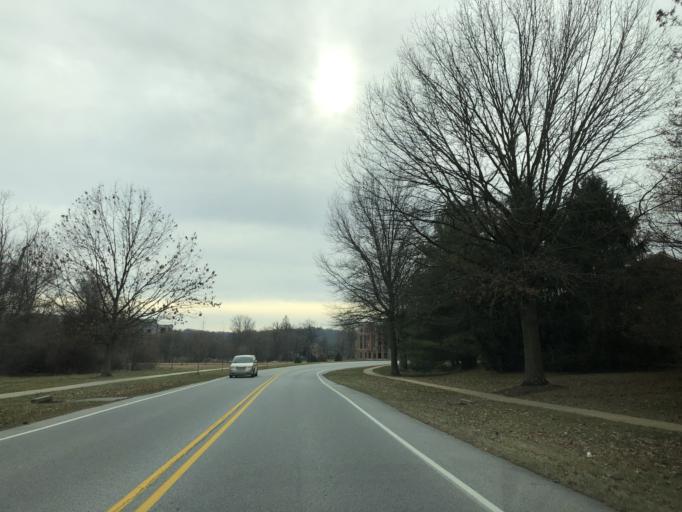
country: US
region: Pennsylvania
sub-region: Chester County
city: Exton
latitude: 40.0307
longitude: -75.6372
